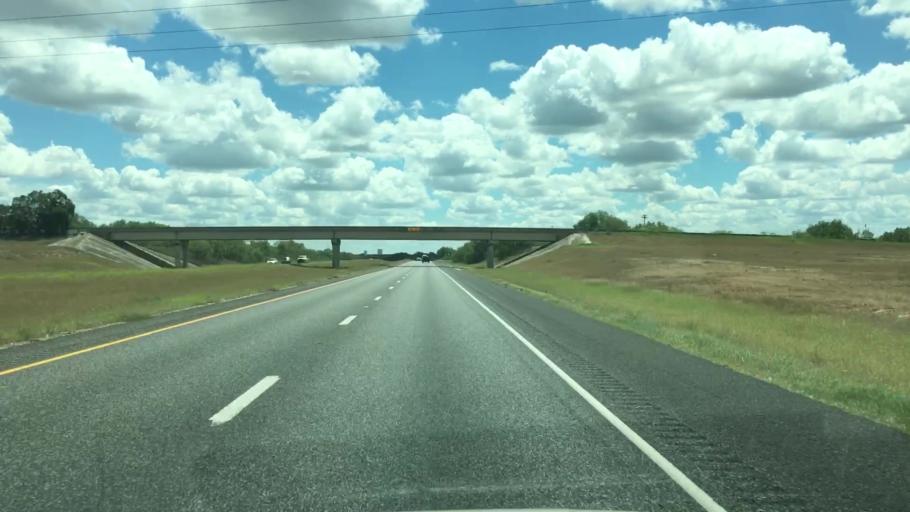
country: US
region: Texas
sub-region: Atascosa County
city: Pleasanton
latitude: 28.9177
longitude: -98.4350
